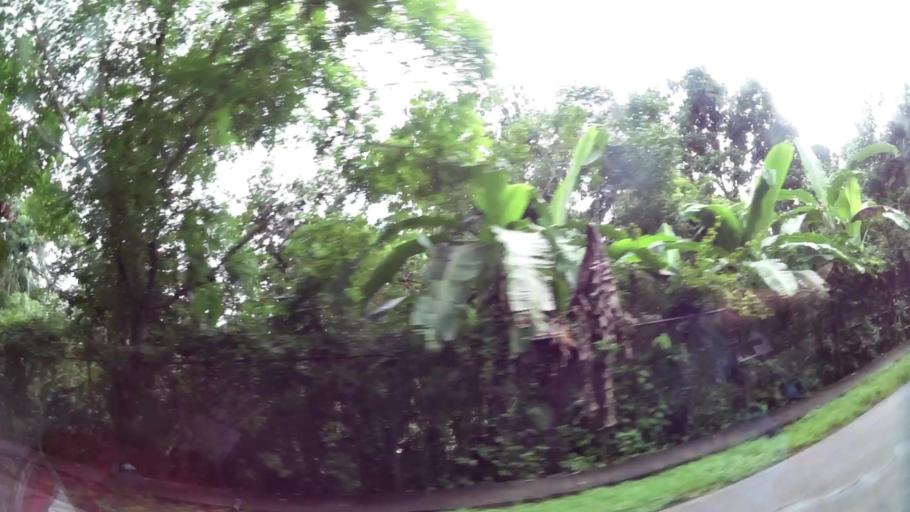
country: PA
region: Panama
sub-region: Distrito de Panama
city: Ancon
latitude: 9.0011
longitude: -79.5754
